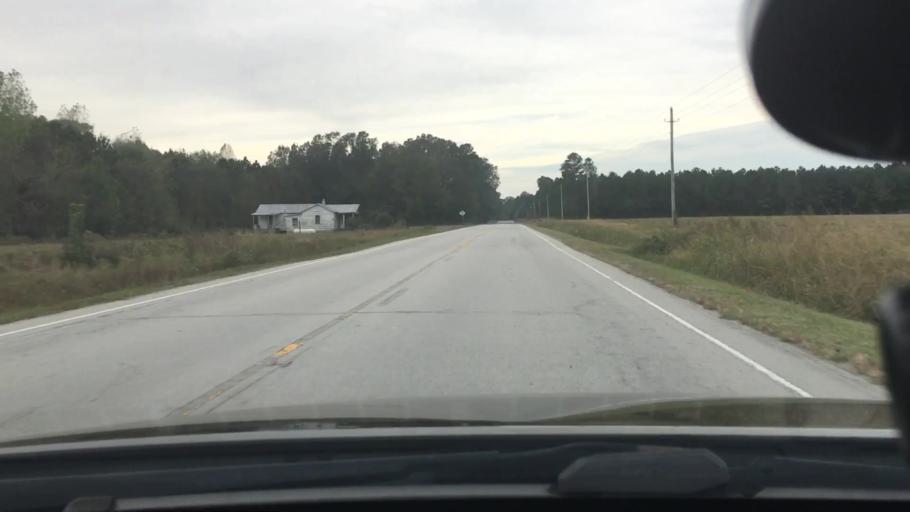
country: US
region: North Carolina
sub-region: Craven County
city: Vanceboro
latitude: 35.4015
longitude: -77.2387
